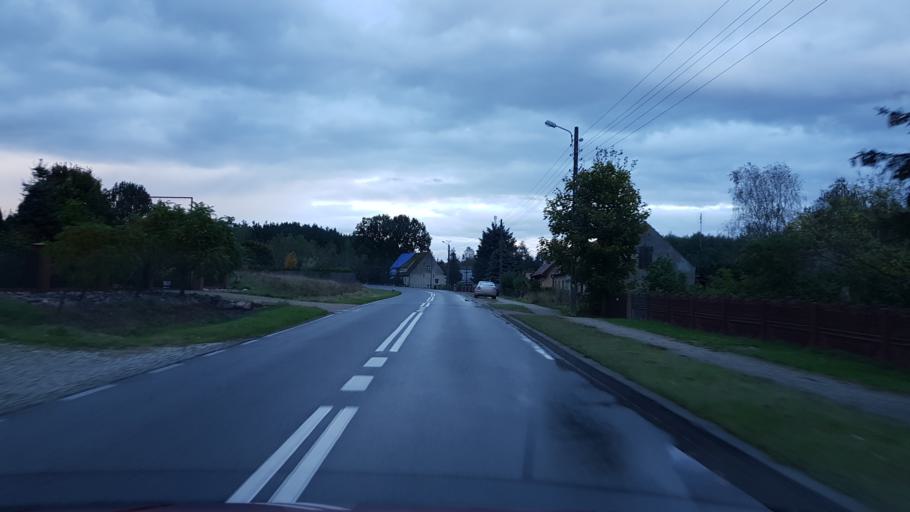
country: PL
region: Greater Poland Voivodeship
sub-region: Powiat pilski
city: Smilowo
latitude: 53.2266
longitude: 16.8754
